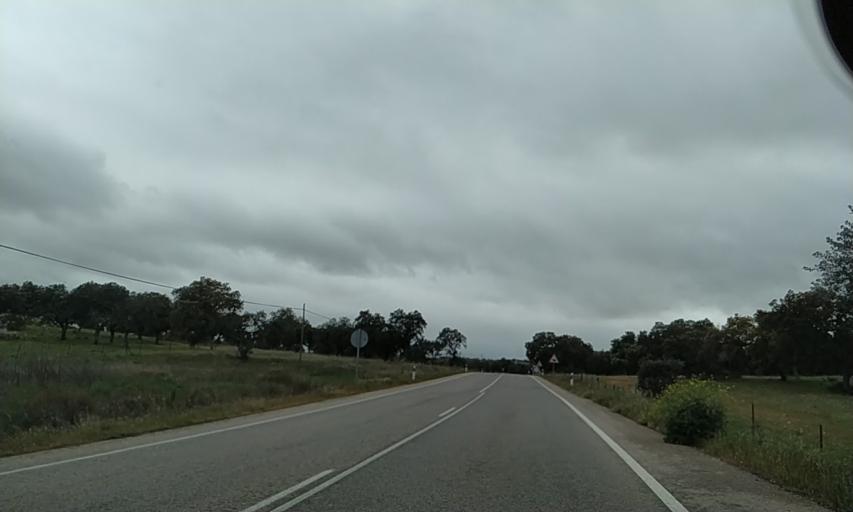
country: ES
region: Extremadura
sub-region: Provincia de Caceres
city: Malpartida de Caceres
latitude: 39.3958
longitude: -6.4256
